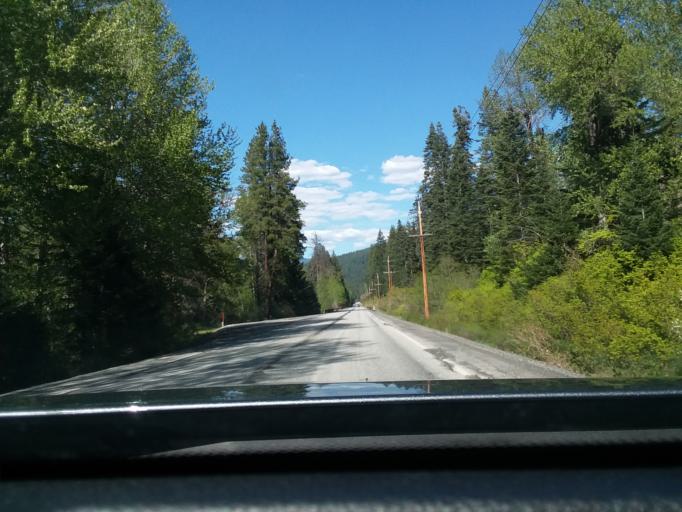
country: US
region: Washington
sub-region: Chelan County
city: Leavenworth
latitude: 47.7651
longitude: -120.7284
